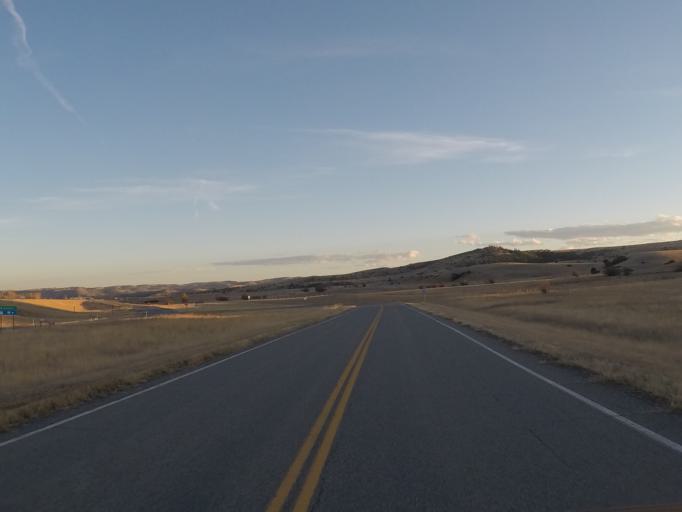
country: US
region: Montana
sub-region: Sweet Grass County
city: Big Timber
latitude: 45.7703
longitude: -109.7961
